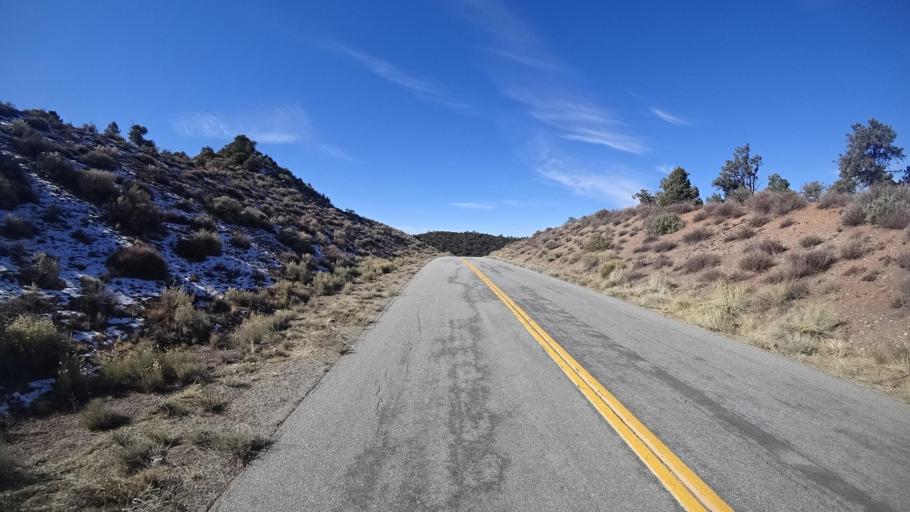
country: US
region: California
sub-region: Kern County
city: Pine Mountain Club
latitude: 34.8638
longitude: -119.2487
